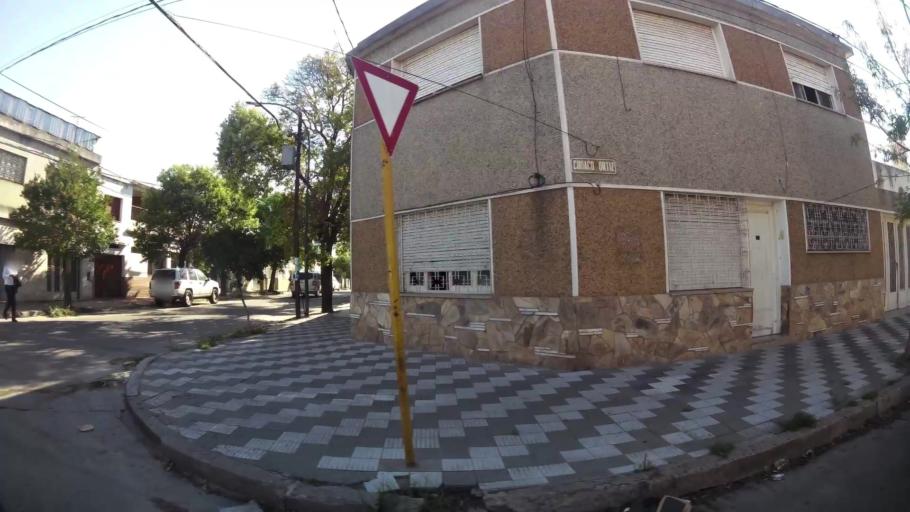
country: AR
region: Cordoba
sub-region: Departamento de Capital
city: Cordoba
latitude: -31.3970
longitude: -64.1529
